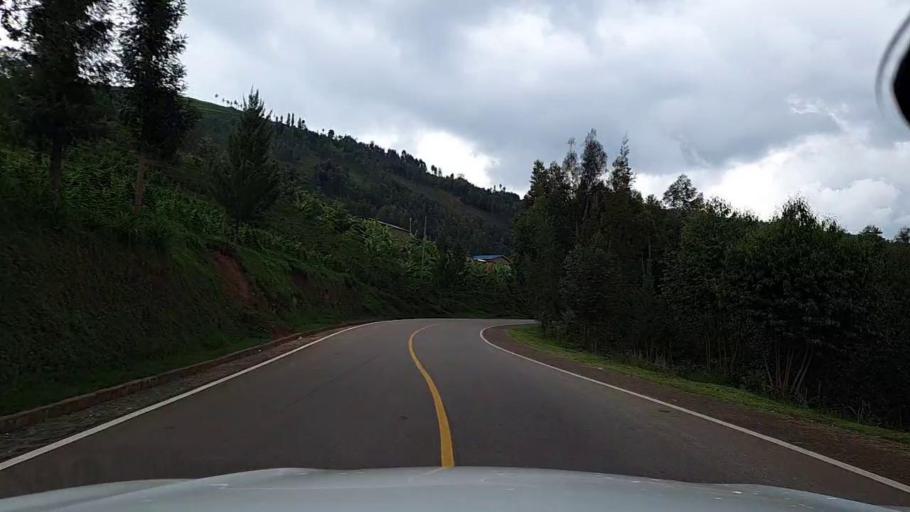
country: RW
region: Northern Province
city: Byumba
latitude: -1.6761
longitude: 30.0965
